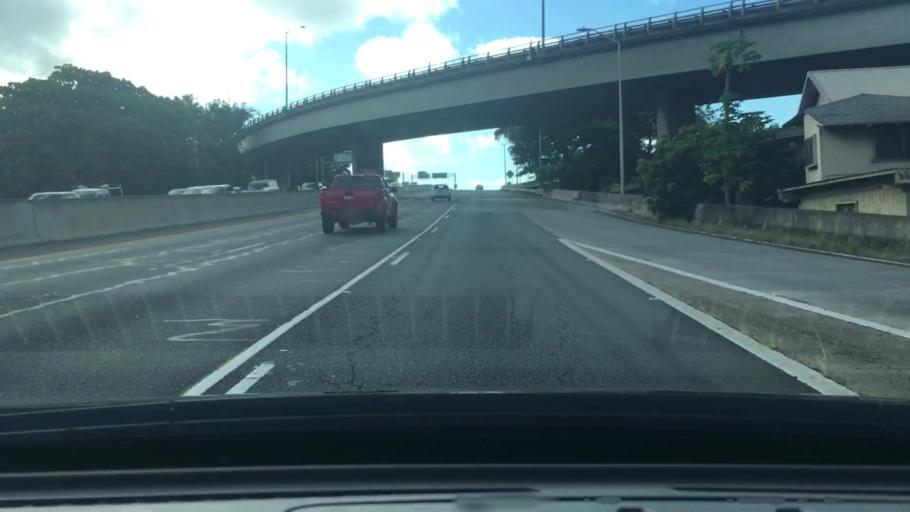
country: US
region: Hawaii
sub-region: Honolulu County
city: Honolulu
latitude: 21.2899
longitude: -157.8163
